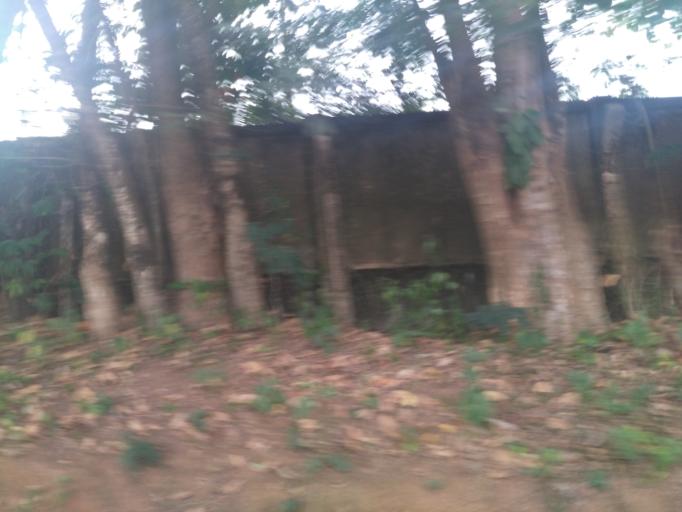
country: GH
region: Ashanti
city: Kumasi
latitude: 6.6779
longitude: -1.6170
